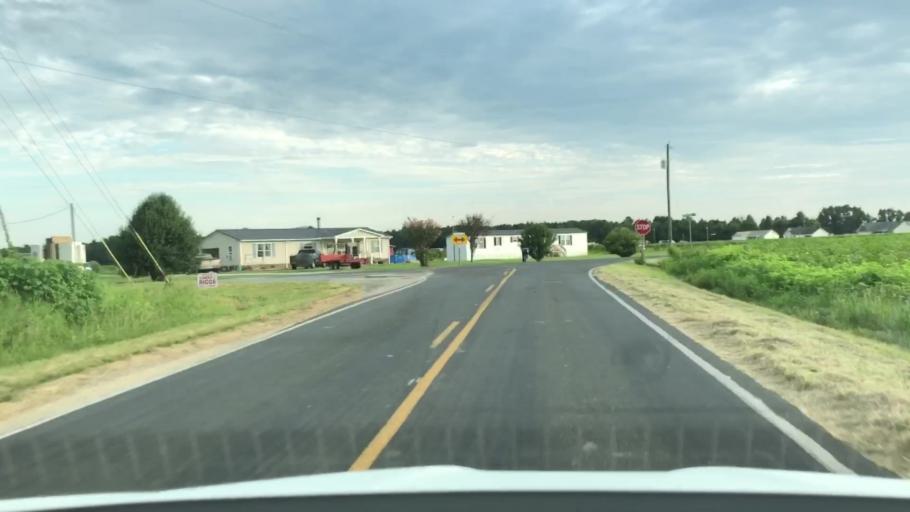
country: US
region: North Carolina
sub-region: Jones County
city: Trenton
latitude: 34.9955
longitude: -77.2805
